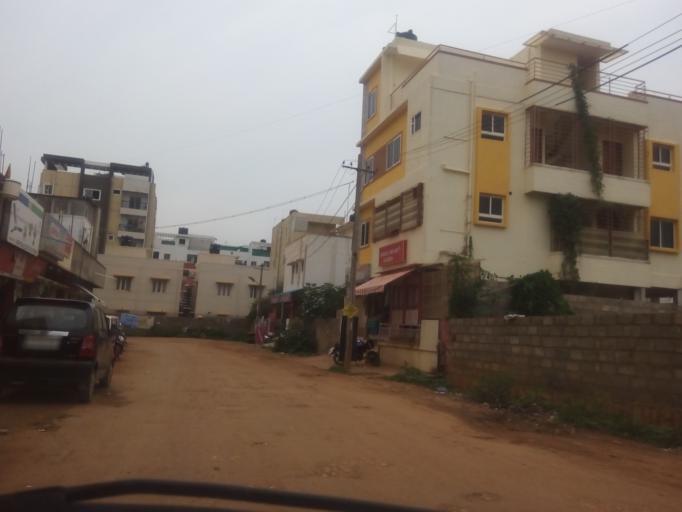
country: IN
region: Karnataka
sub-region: Bangalore Urban
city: Anekal
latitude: 12.8348
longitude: 77.6972
